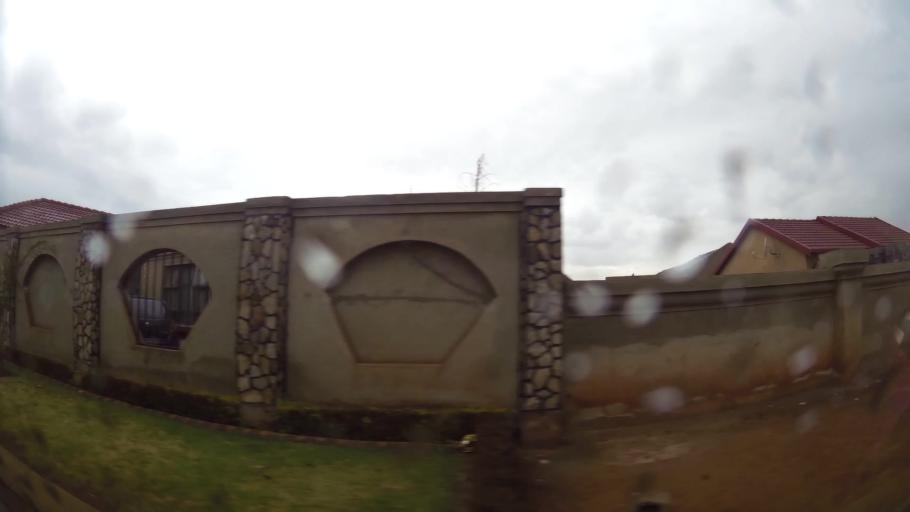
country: ZA
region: Gauteng
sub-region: Ekurhuleni Metropolitan Municipality
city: Germiston
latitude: -26.3321
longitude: 28.2035
